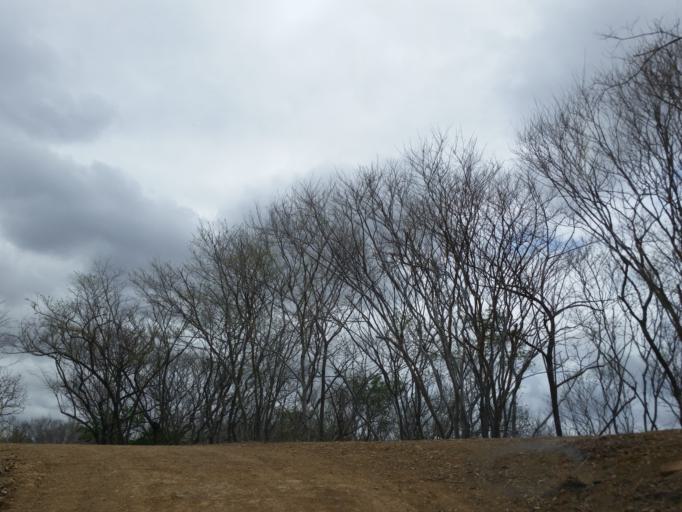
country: NI
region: Rivas
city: Tola
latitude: 11.4158
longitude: -86.0619
